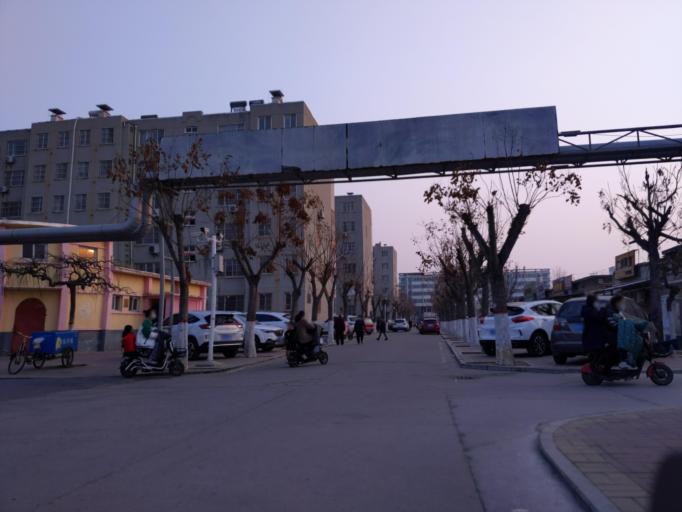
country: CN
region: Henan Sheng
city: Zhongyuanlu
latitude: 35.7720
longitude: 115.0886
